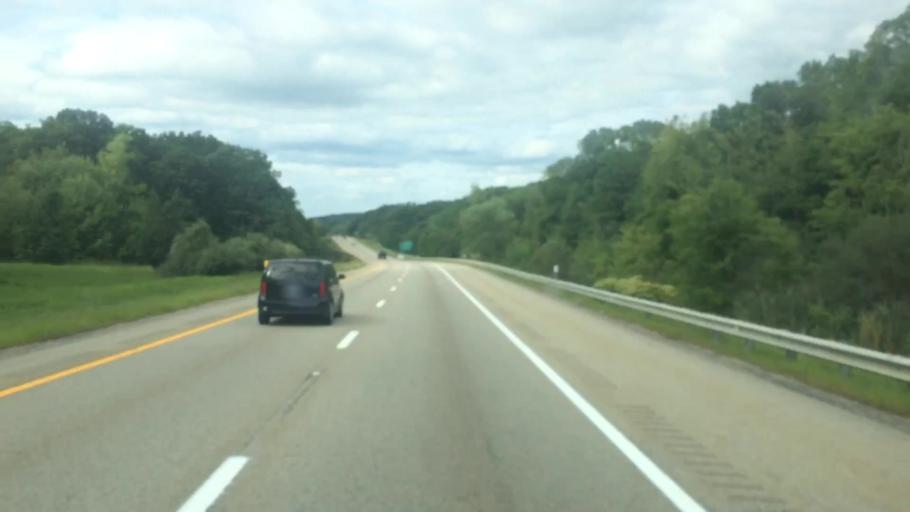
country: US
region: Rhode Island
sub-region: Providence County
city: Cumberland Hill
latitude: 41.9504
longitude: -71.4818
